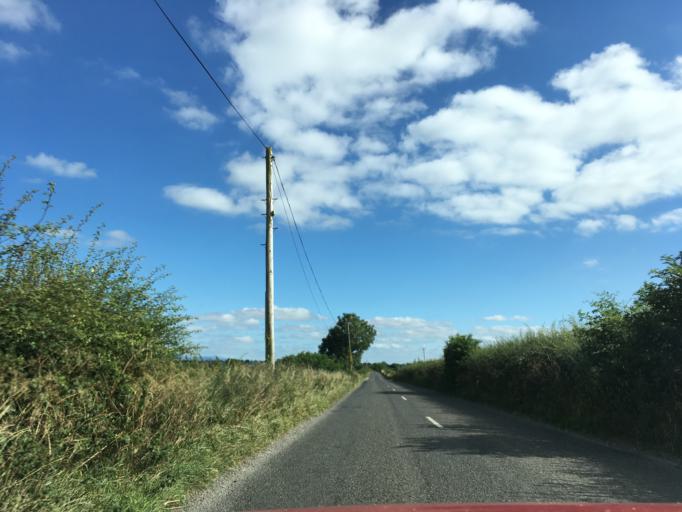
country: IE
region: Munster
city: Cashel
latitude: 52.4707
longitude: -7.9222
